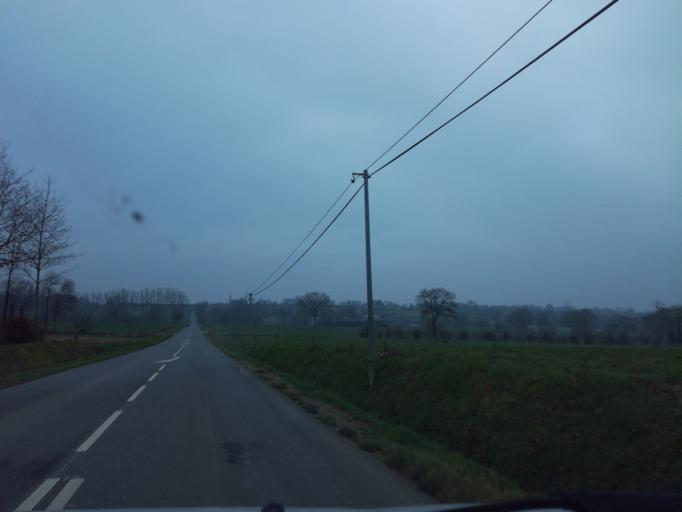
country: FR
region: Brittany
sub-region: Departement d'Ille-et-Vilaine
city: Gosne
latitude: 48.2569
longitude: -1.4537
